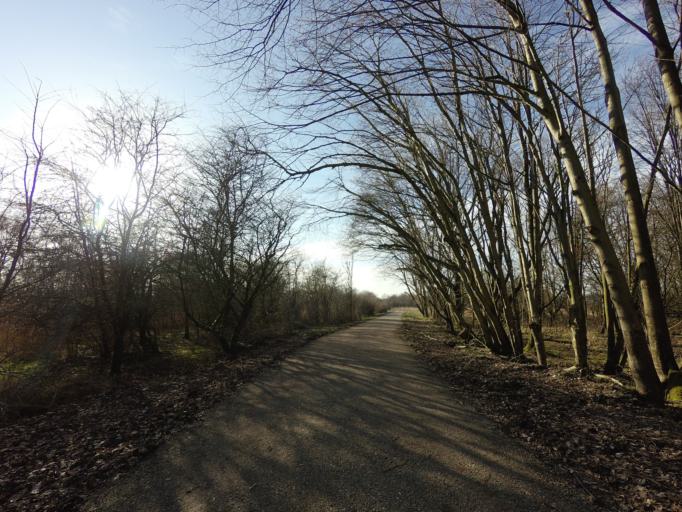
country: NL
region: North Holland
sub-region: Gemeente Naarden
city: Naarden
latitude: 52.3352
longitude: 5.1751
